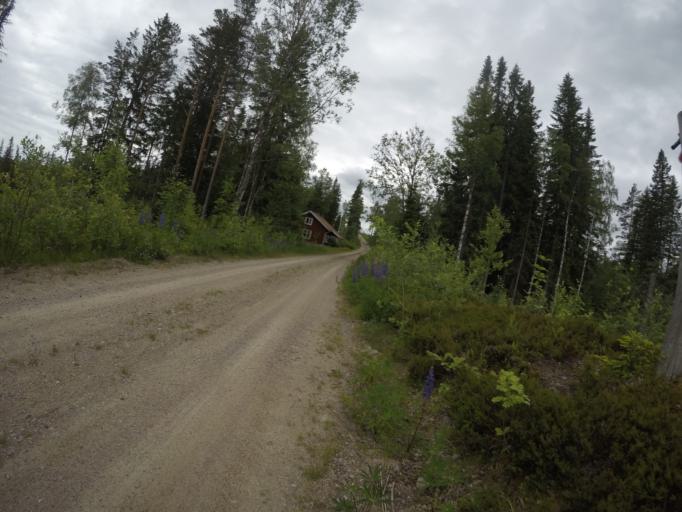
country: SE
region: Dalarna
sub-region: Ludvika Kommun
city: Abborrberget
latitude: 60.0826
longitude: 14.5547
